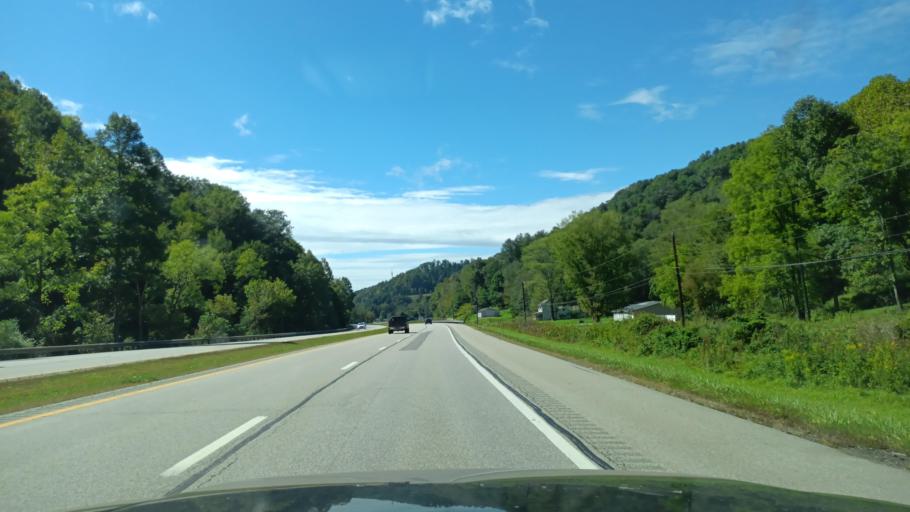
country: US
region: West Virginia
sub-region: Harrison County
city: Salem
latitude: 39.2966
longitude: -80.6213
